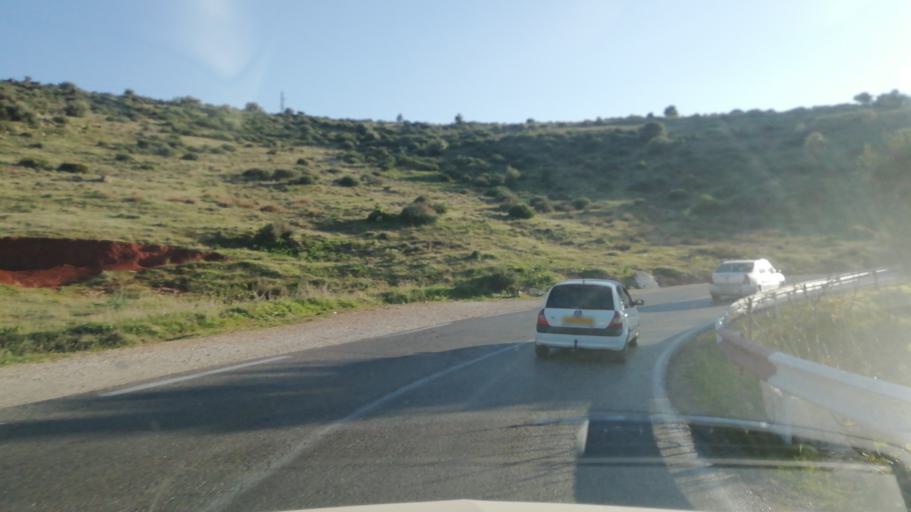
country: DZ
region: Tlemcen
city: Beni Mester
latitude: 34.8534
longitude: -1.4488
